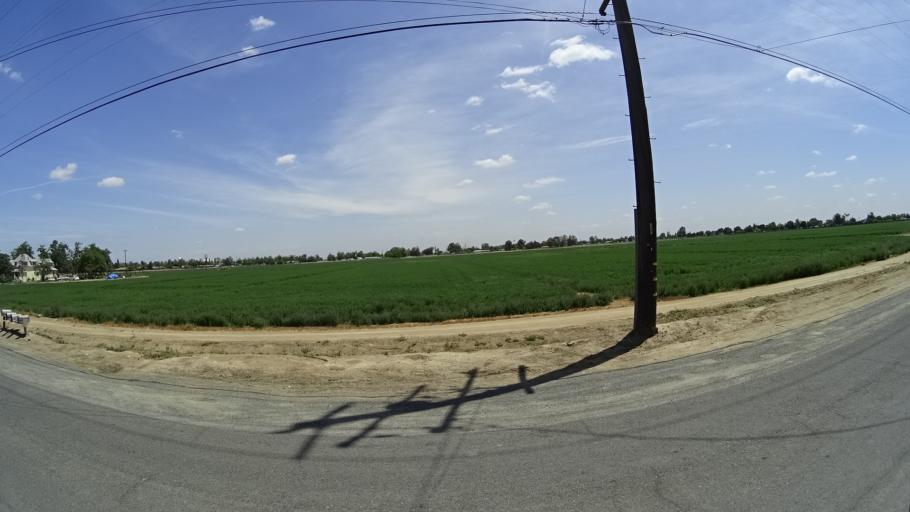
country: US
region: California
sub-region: Kings County
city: Home Garden
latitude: 36.3064
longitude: -119.6460
